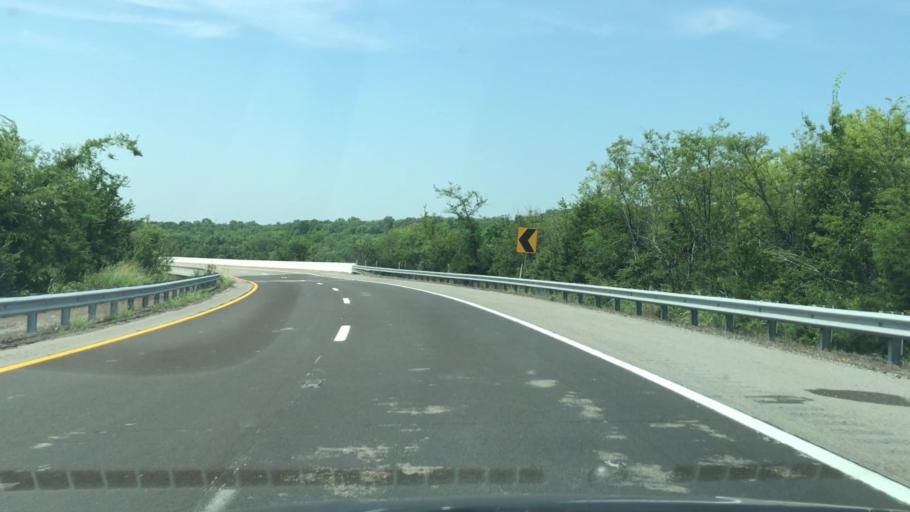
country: US
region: Tennessee
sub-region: Wilson County
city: Lebanon
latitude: 36.1848
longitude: -86.3535
